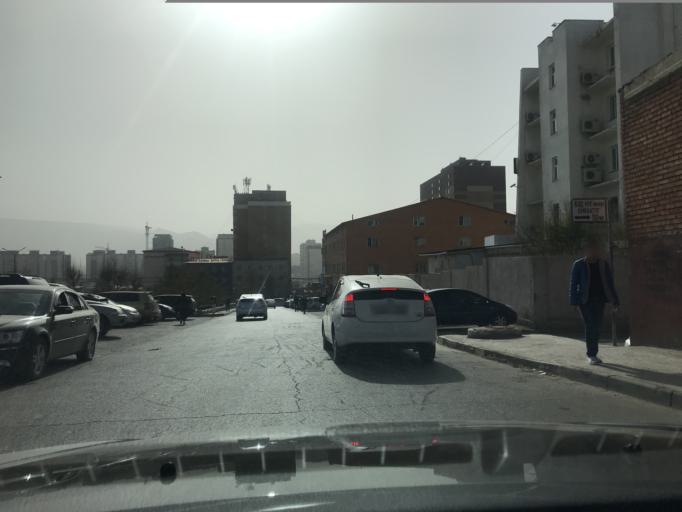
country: MN
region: Ulaanbaatar
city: Ulaanbaatar
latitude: 47.9188
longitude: 106.9522
